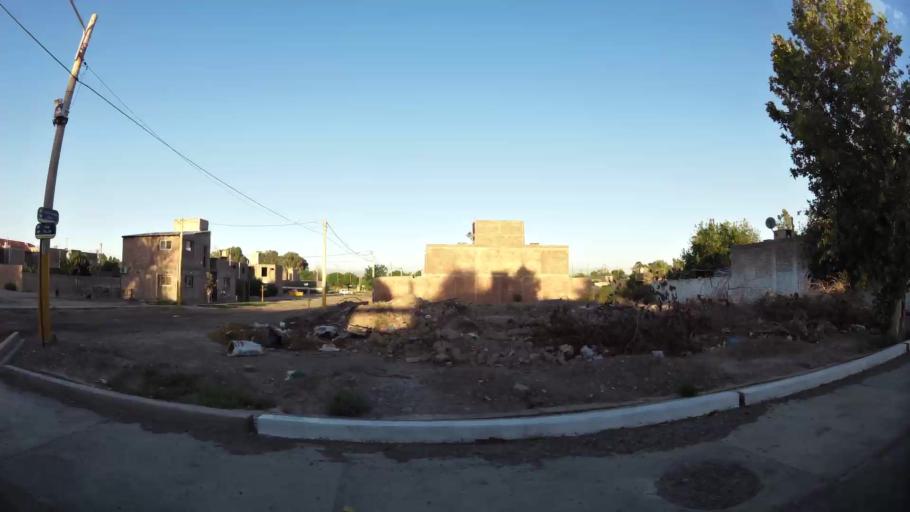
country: AR
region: San Juan
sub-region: Departamento de Santa Lucia
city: Santa Lucia
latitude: -31.5316
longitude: -68.5070
